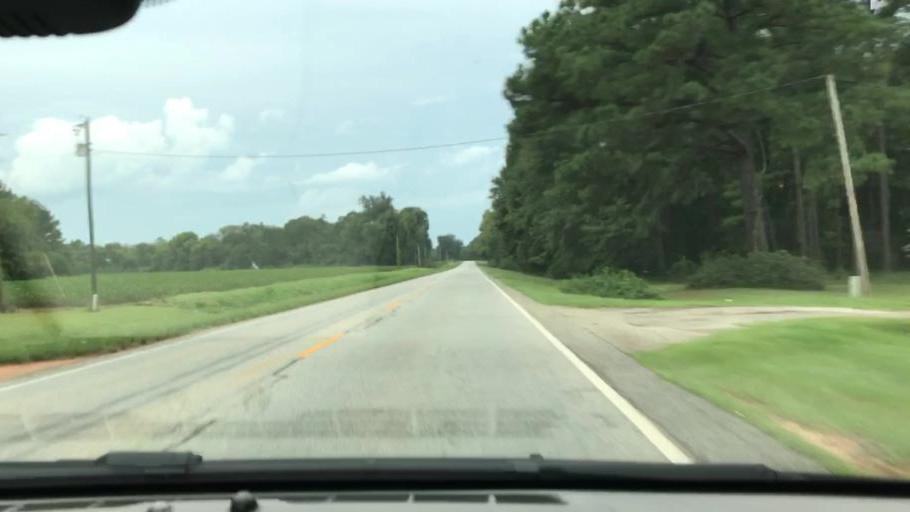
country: US
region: Georgia
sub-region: Early County
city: Blakely
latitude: 31.3254
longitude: -85.0173
